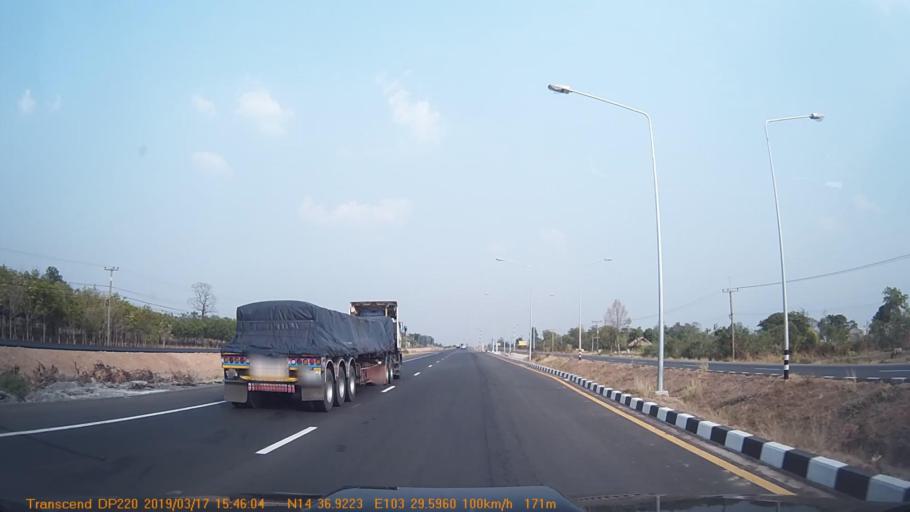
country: TH
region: Surin
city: Prasat
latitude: 14.6152
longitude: 103.4937
